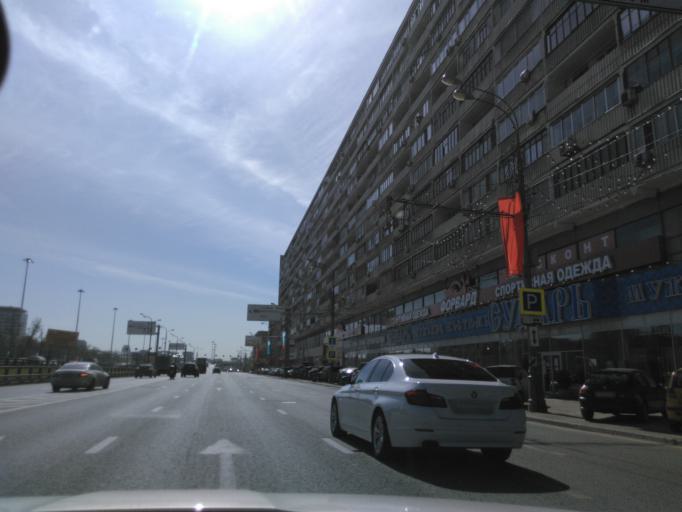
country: RU
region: Moskovskaya
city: Presnenskiy
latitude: 55.7892
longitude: 37.5565
